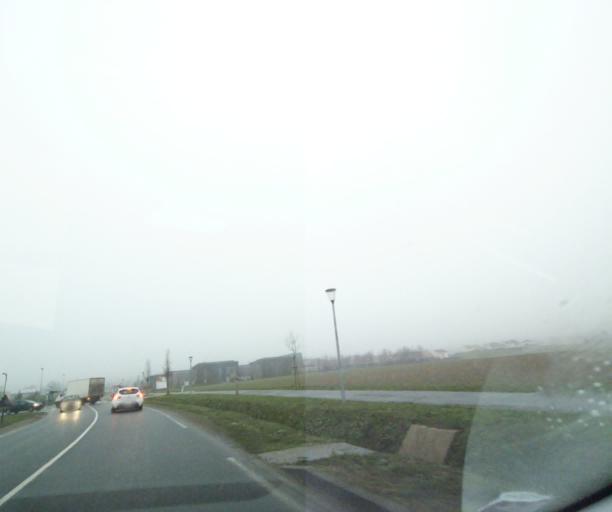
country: FR
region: Ile-de-France
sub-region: Departement de Seine-et-Marne
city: Othis
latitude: 49.0678
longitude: 2.6803
